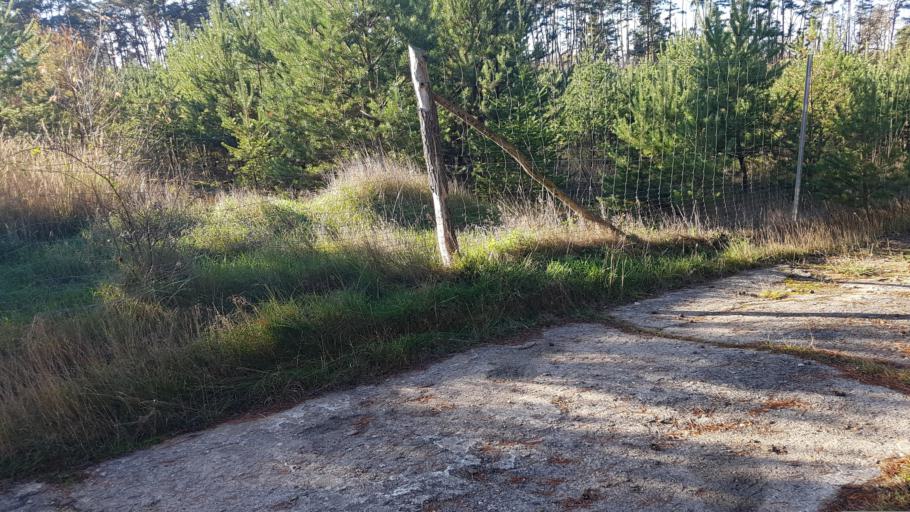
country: DE
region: Brandenburg
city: Schlieben
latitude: 51.7401
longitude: 13.3868
